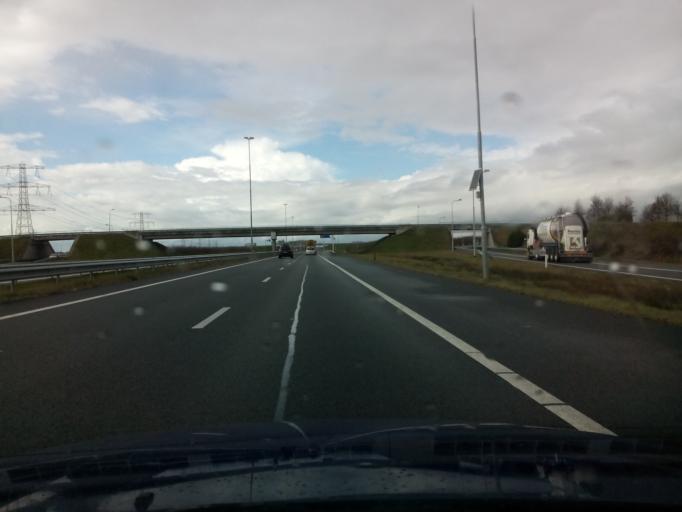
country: NL
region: Drenthe
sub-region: Gemeente Coevorden
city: Sleen
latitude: 52.7261
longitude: 6.7973
